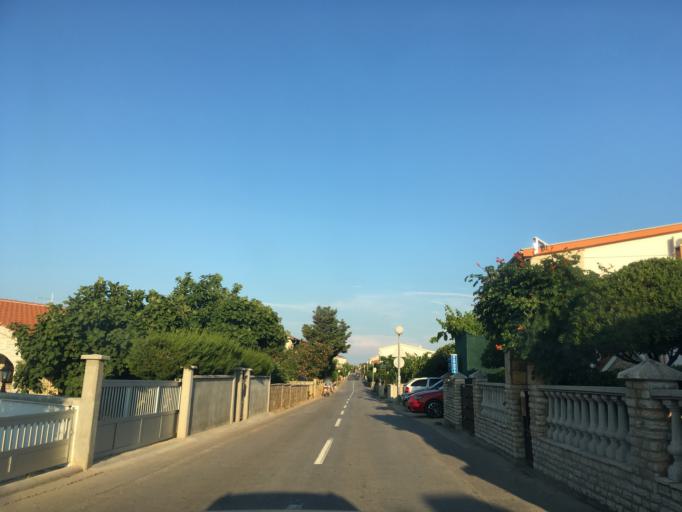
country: HR
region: Zadarska
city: Vir
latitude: 44.3066
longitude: 15.0886
